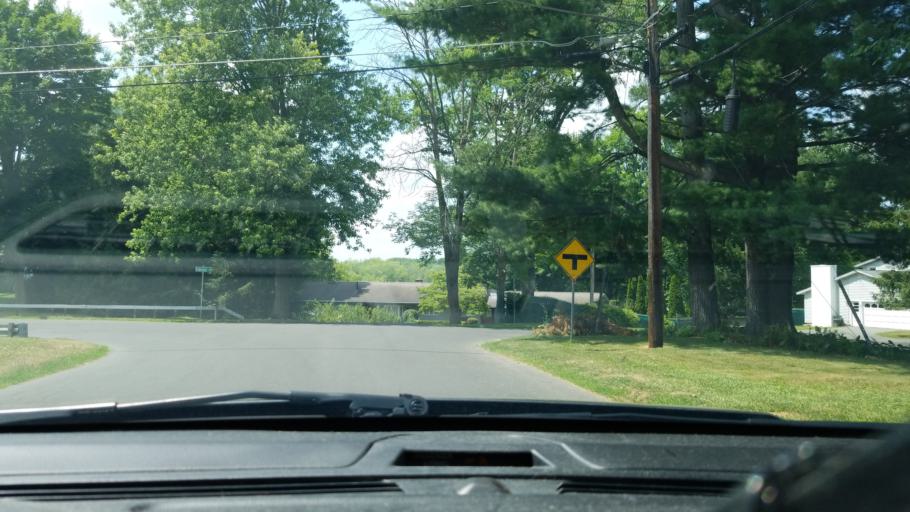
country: US
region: New York
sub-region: Onondaga County
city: Liverpool
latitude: 43.1374
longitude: -76.2362
